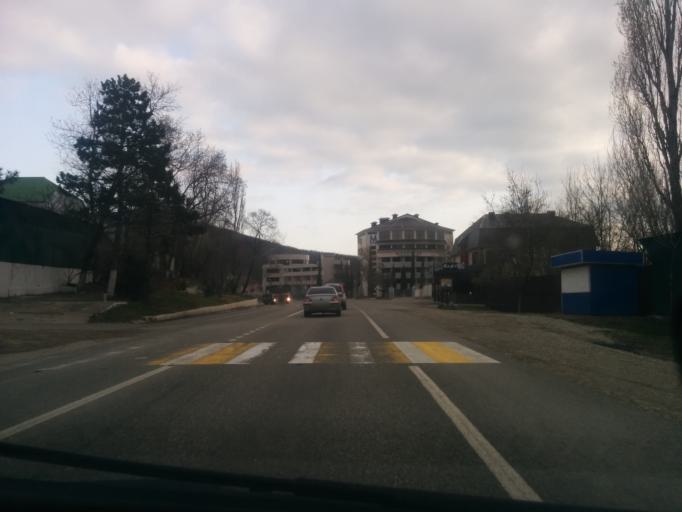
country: RU
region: Krasnodarskiy
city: Agoy
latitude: 44.1420
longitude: 39.0226
